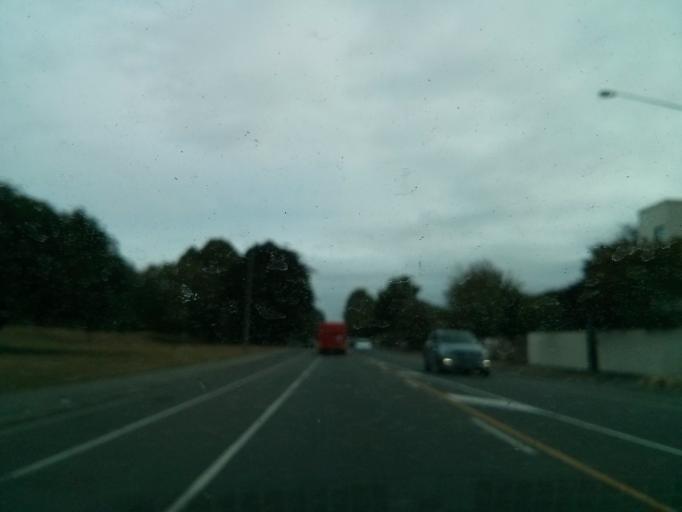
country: NZ
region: Canterbury
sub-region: Christchurch City
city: Christchurch
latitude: -43.5260
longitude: 172.5874
